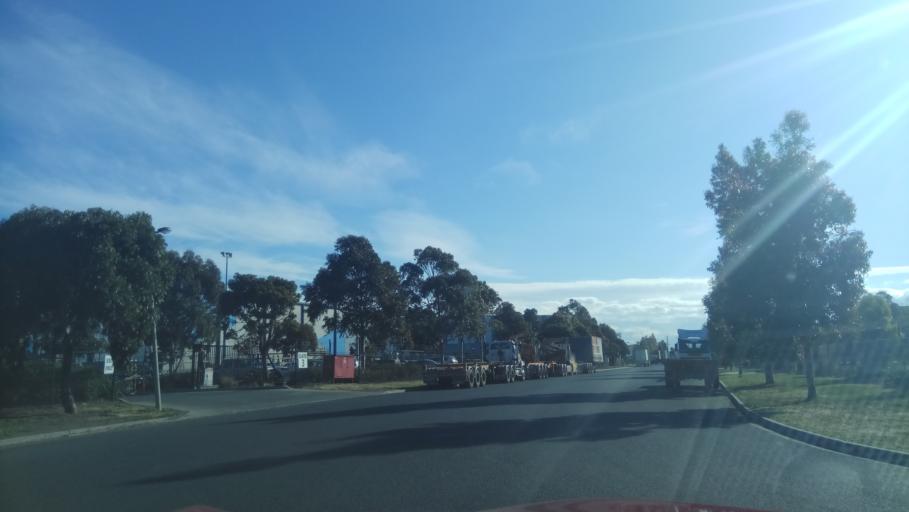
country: AU
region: Victoria
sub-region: Hobsons Bay
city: Altona North
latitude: -37.8474
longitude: 144.8303
